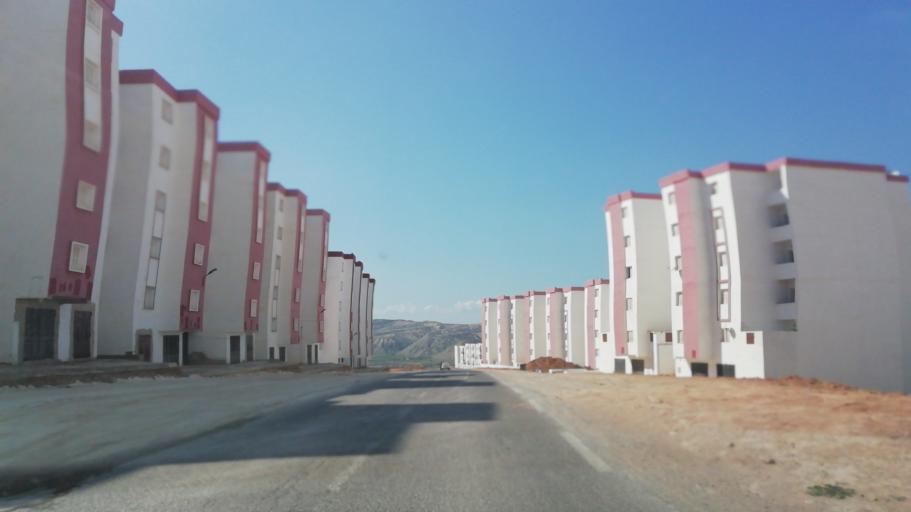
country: DZ
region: Mascara
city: Mascara
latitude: 35.5561
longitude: 0.0706
